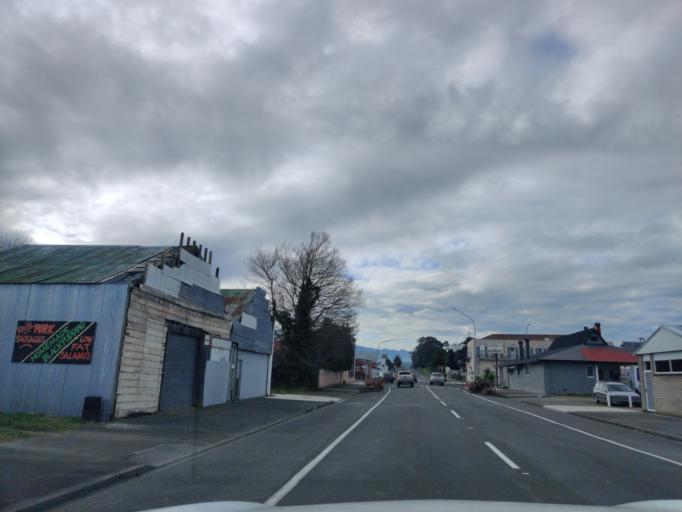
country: NZ
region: Manawatu-Wanganui
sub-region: Palmerston North City
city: Palmerston North
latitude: -40.3379
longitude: 175.8664
